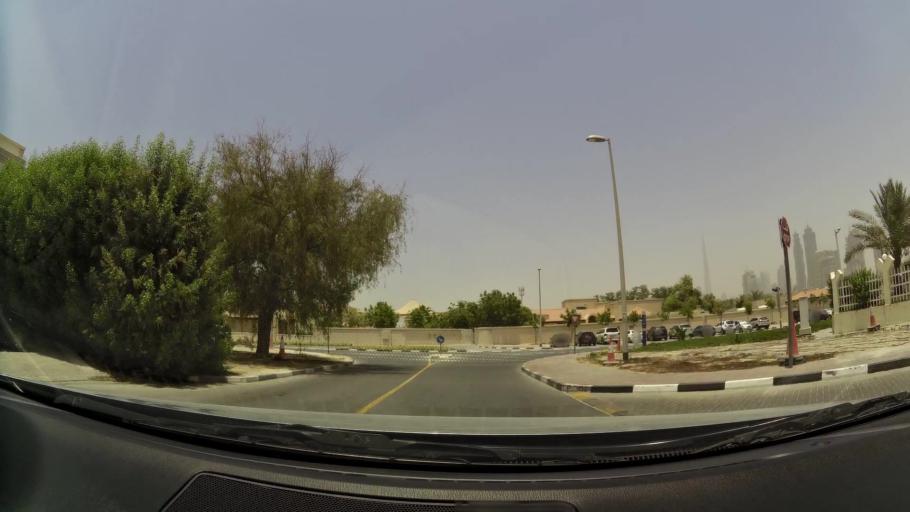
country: AE
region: Dubai
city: Dubai
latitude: 25.1821
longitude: 55.2404
